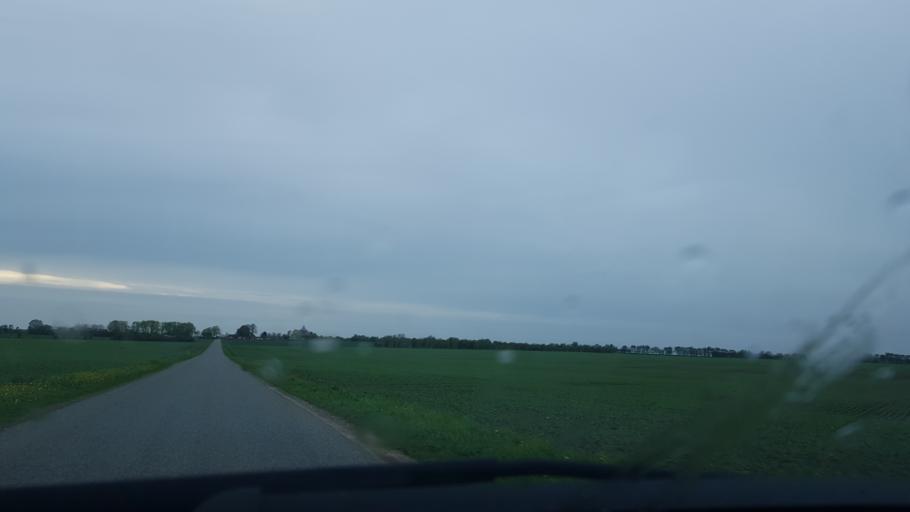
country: DK
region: South Denmark
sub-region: Vejen Kommune
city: Rodding
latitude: 55.4066
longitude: 9.1178
